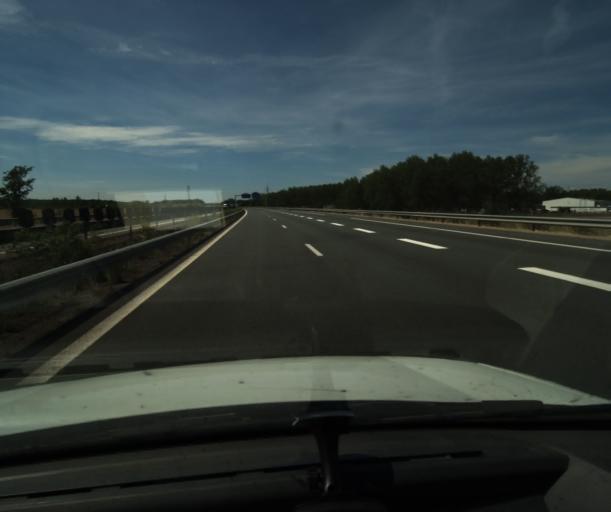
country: FR
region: Midi-Pyrenees
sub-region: Departement du Tarn-et-Garonne
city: Campsas
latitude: 43.9224
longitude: 1.3155
